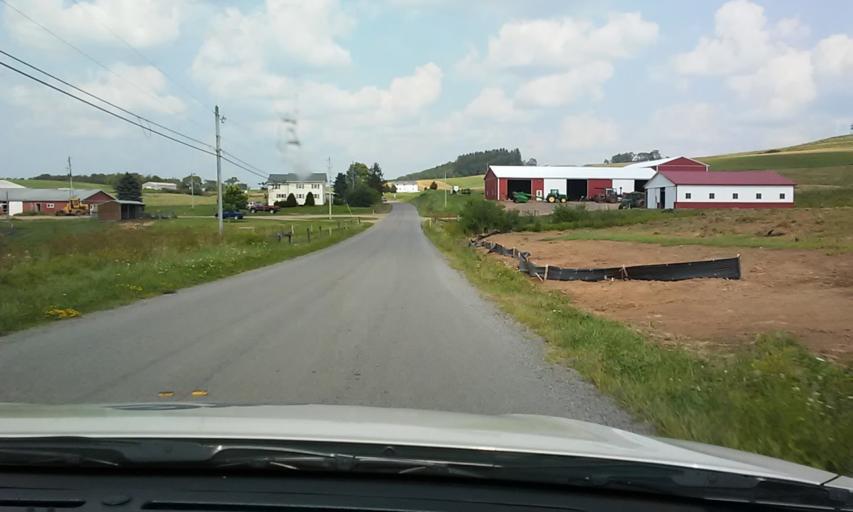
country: US
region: Pennsylvania
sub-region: Potter County
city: Coudersport
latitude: 41.8062
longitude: -77.8621
